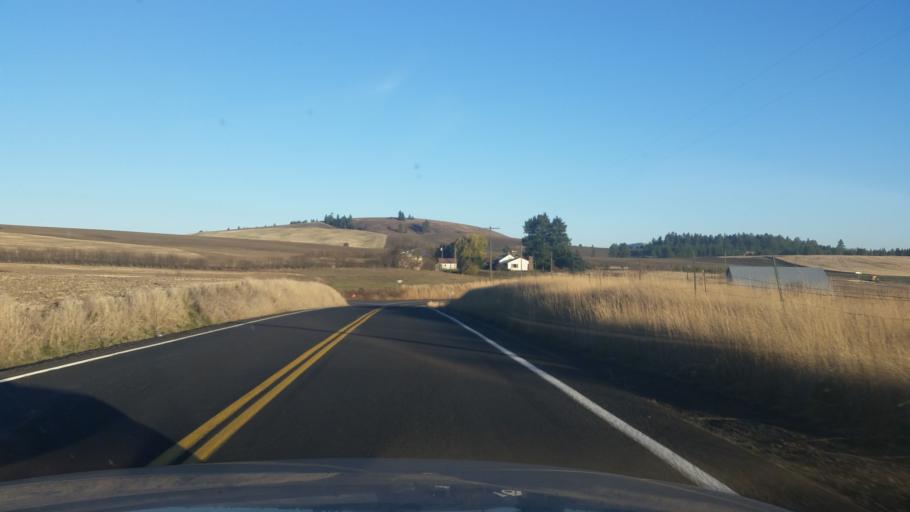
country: US
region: Washington
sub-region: Spokane County
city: Opportunity
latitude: 47.3503
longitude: -117.2331
